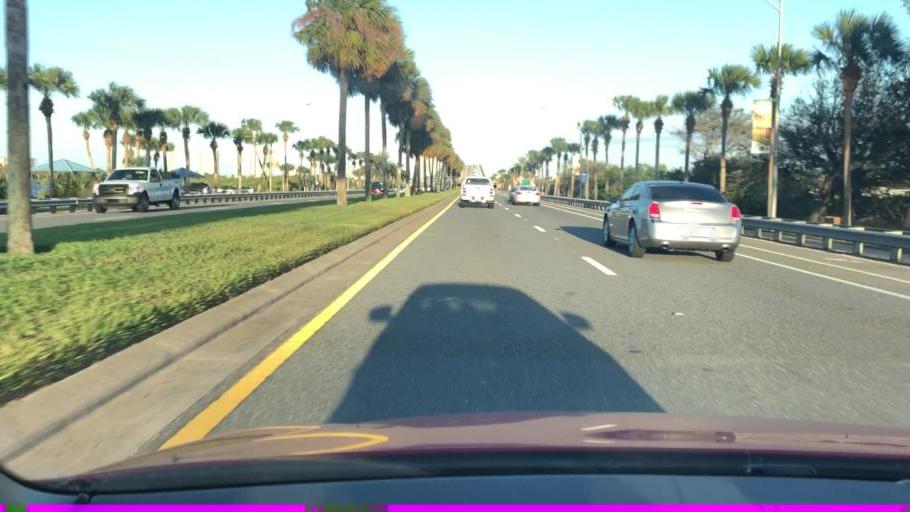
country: US
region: Florida
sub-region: Volusia County
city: Port Orange
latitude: 29.1451
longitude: -80.9822
